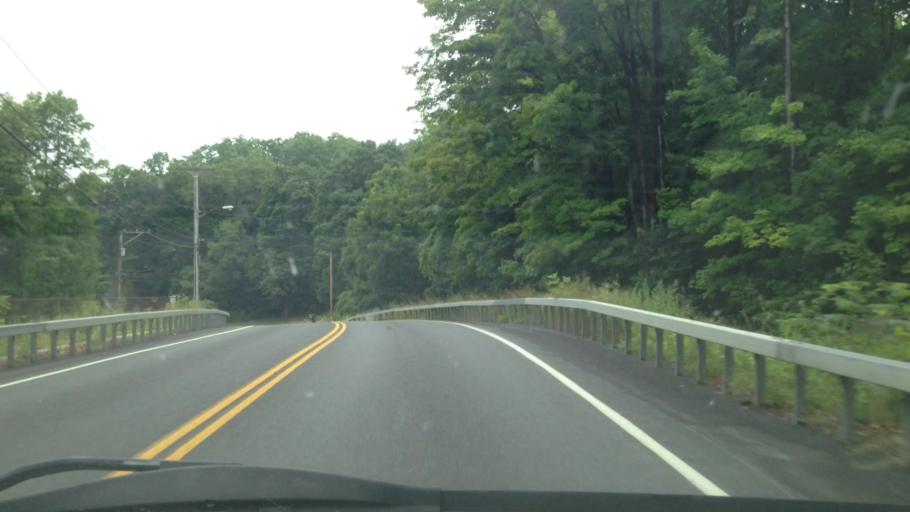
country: US
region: New York
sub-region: Ulster County
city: Highland
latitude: 41.7367
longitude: -74.0059
